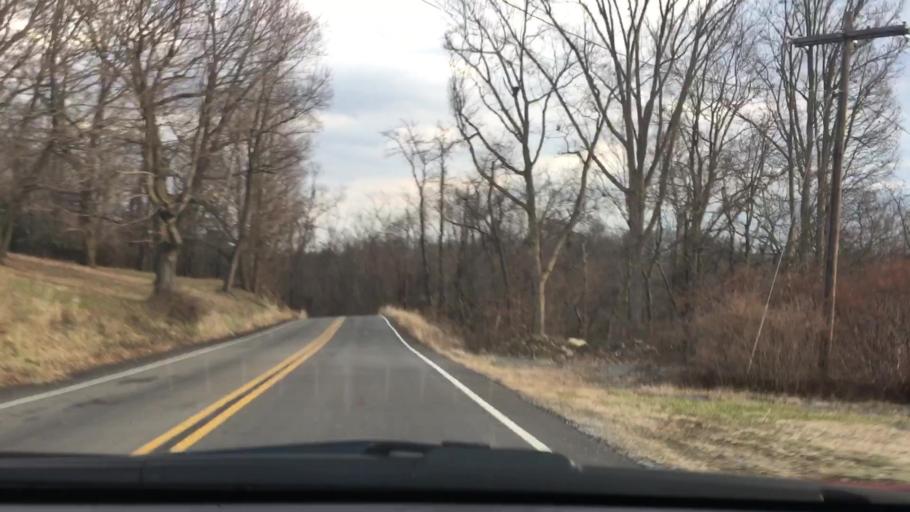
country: US
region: Pennsylvania
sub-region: Allegheny County
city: Lincoln
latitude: 40.2965
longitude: -79.8467
